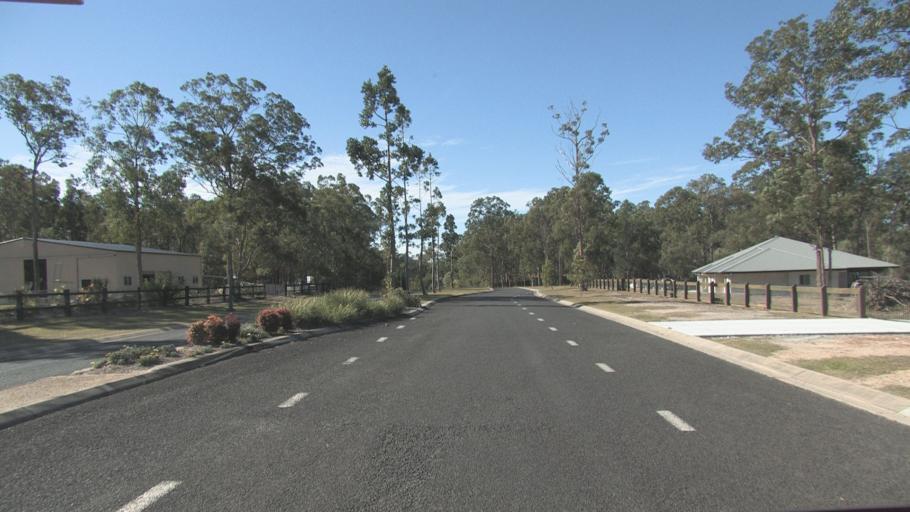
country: AU
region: Queensland
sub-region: Ipswich
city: Springfield Lakes
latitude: -27.7347
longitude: 152.9215
